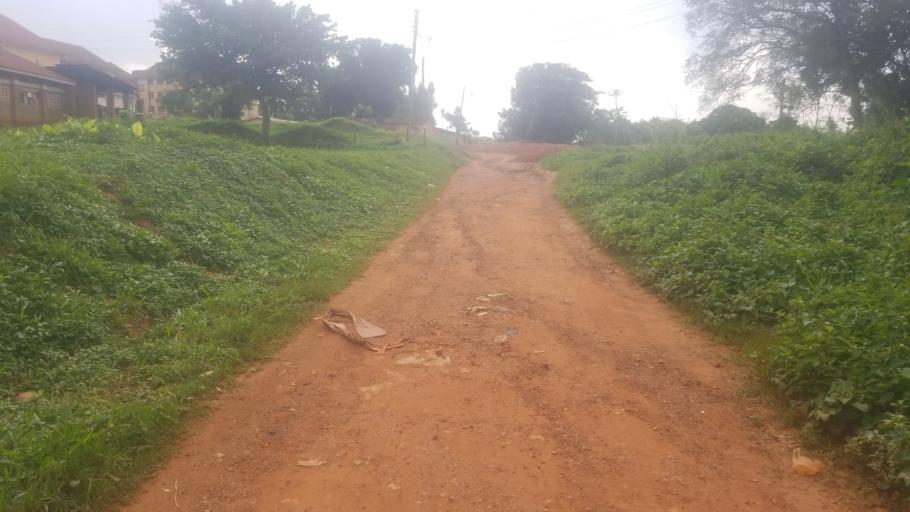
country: UG
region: Central Region
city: Kampala Central Division
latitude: 0.3383
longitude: 32.5695
